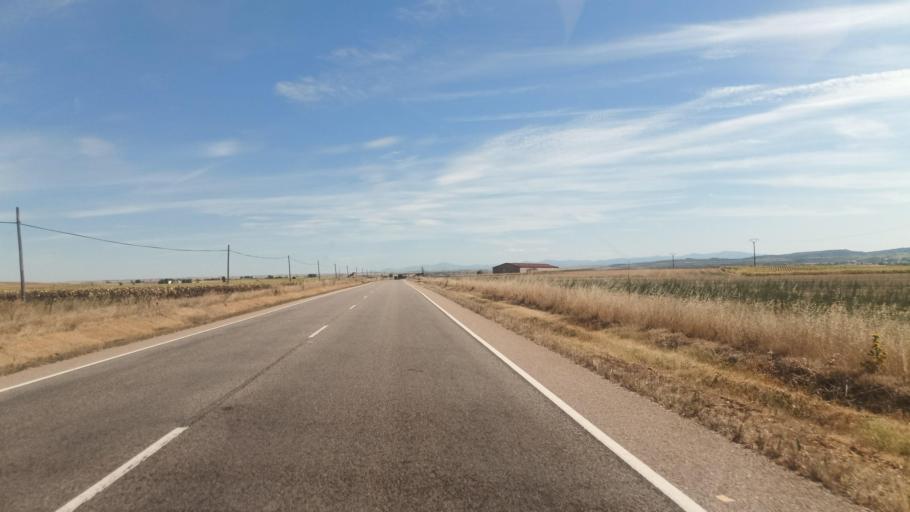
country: ES
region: Castille and Leon
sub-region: Provincia de Burgos
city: Quintanabureba
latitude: 42.6341
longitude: -3.3810
